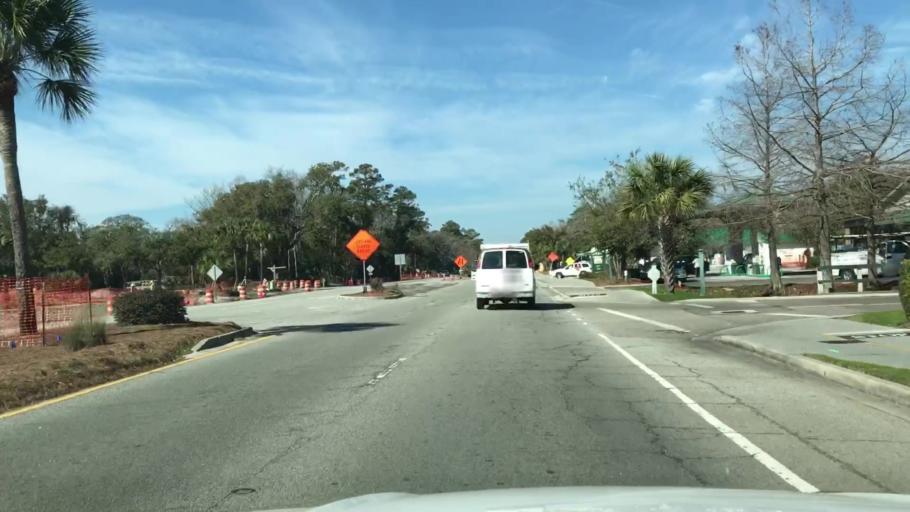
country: US
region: South Carolina
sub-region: Beaufort County
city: Hilton Head Island
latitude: 32.1432
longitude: -80.7522
